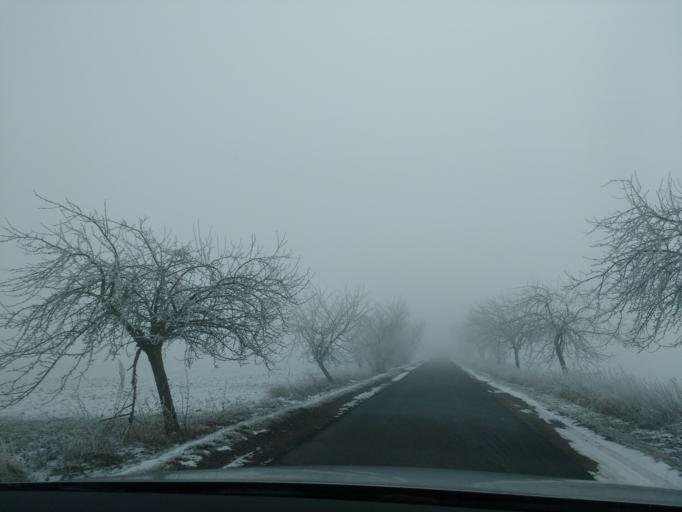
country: DE
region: Saxony-Anhalt
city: Oppin
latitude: 51.5809
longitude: 12.0010
